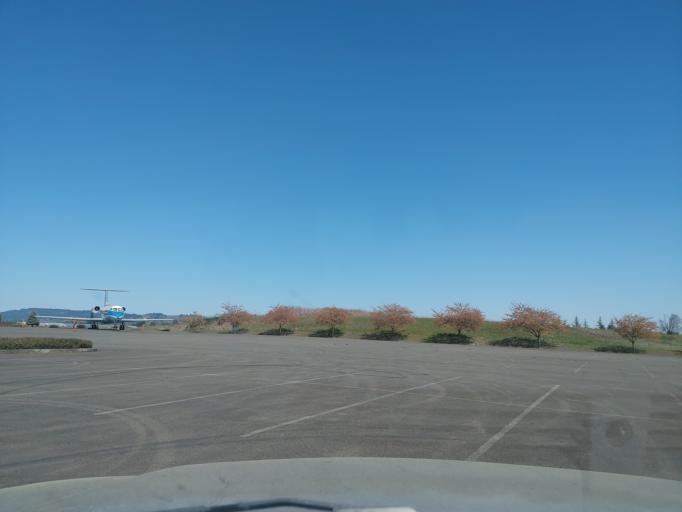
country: US
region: Oregon
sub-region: Yamhill County
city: Lafayette
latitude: 45.2051
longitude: -123.1415
